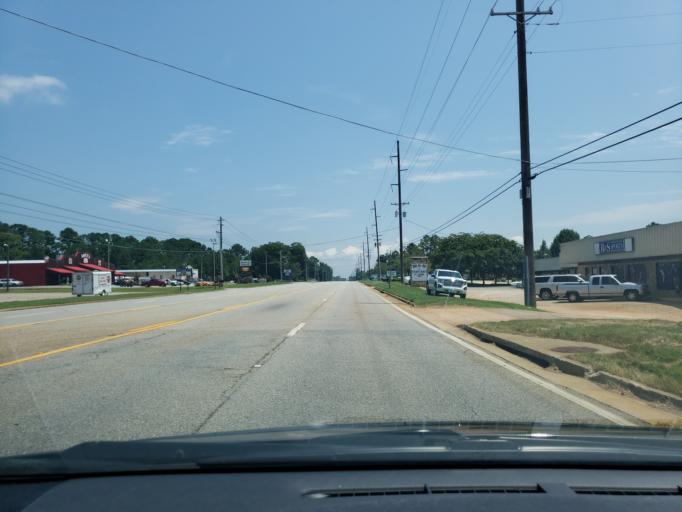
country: US
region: Georgia
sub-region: Dougherty County
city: Albany
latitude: 31.5856
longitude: -84.2353
